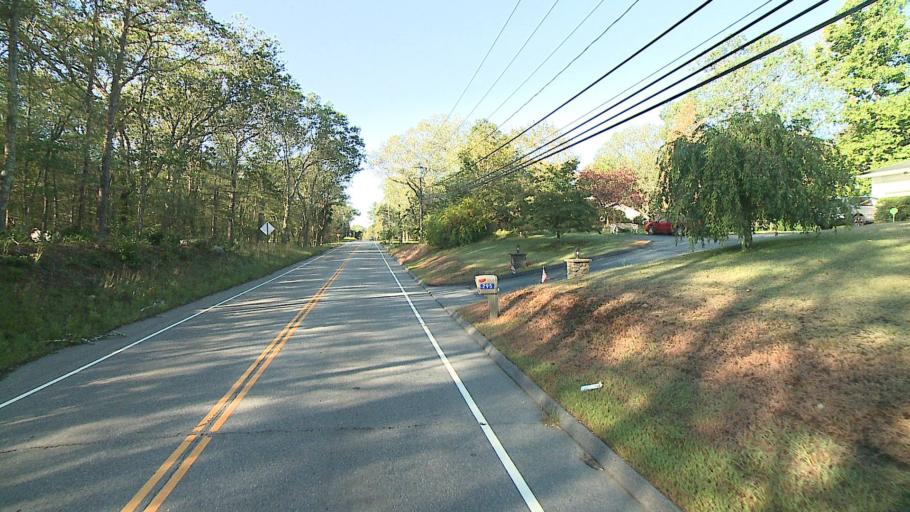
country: US
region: Connecticut
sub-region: Windham County
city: East Brooklyn
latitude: 41.7813
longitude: -71.8911
